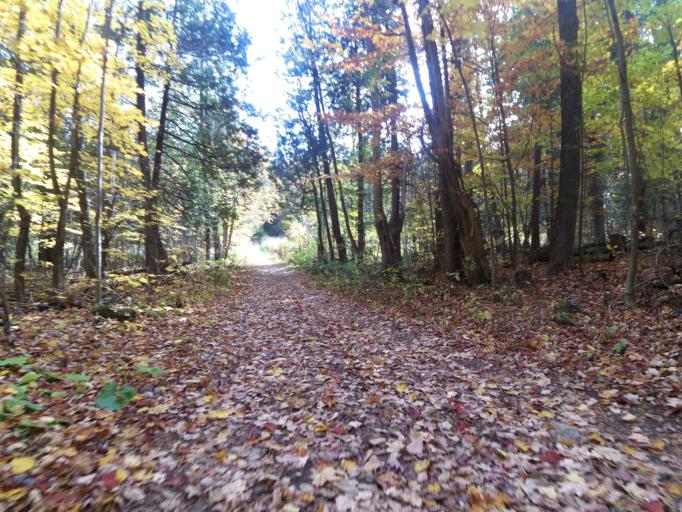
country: CA
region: Quebec
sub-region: Outaouais
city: Gatineau
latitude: 45.4749
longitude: -75.8229
